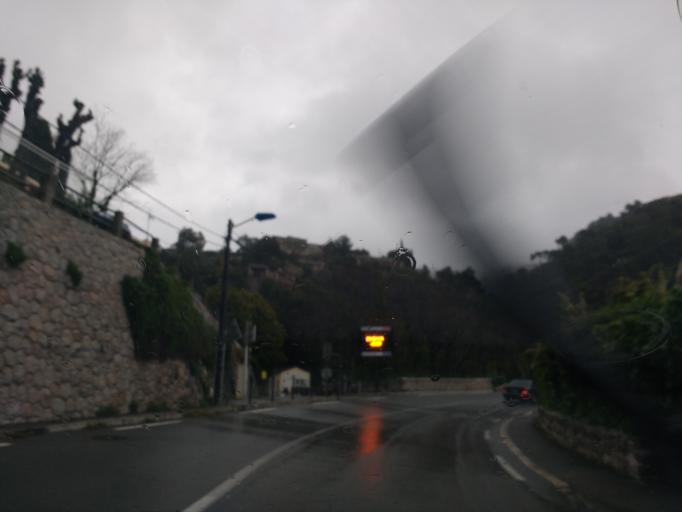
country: FR
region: Provence-Alpes-Cote d'Azur
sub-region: Departement des Alpes-Maritimes
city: Eze
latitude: 43.7253
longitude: 7.3805
